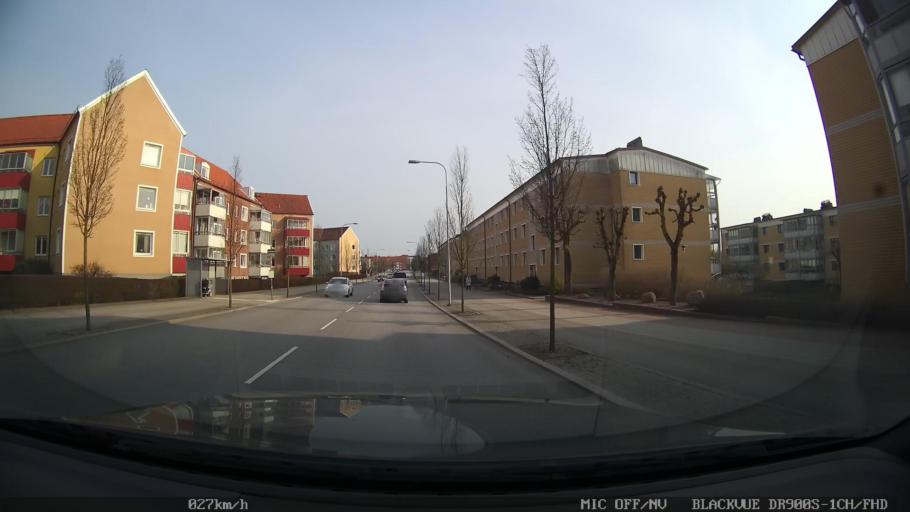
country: SE
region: Skane
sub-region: Ystads Kommun
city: Ystad
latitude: 55.4317
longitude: 13.8031
